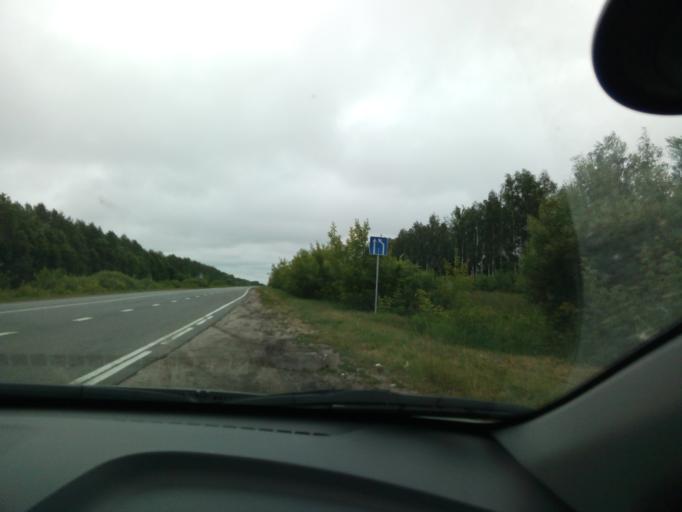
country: RU
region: Chuvashia
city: Alikovo
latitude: 55.6121
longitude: 46.6657
